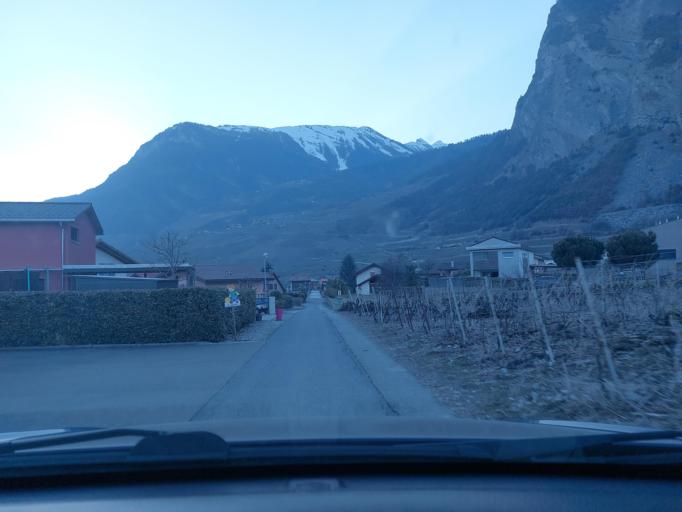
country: CH
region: Valais
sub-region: Martigny District
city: Leytron
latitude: 46.1888
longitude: 7.2144
